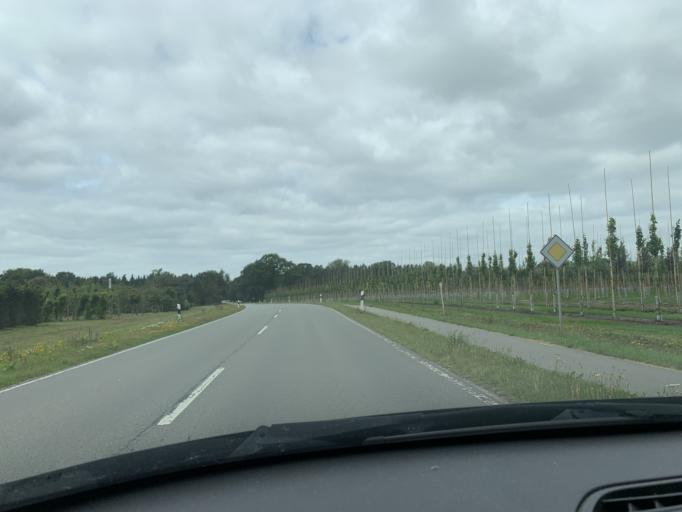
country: DE
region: Lower Saxony
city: Bad Zwischenahn
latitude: 53.2386
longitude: 7.9877
